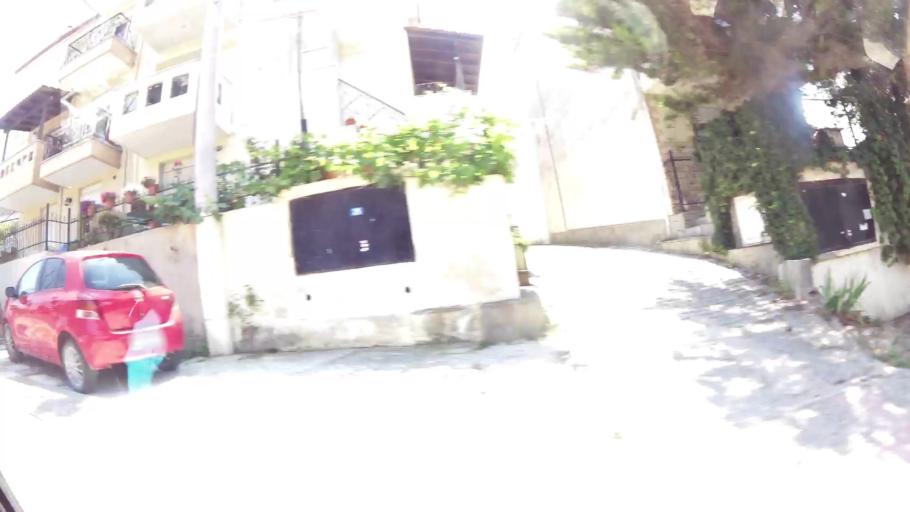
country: GR
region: Central Macedonia
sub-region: Nomos Thessalonikis
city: Trilofos
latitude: 40.4688
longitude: 22.9657
